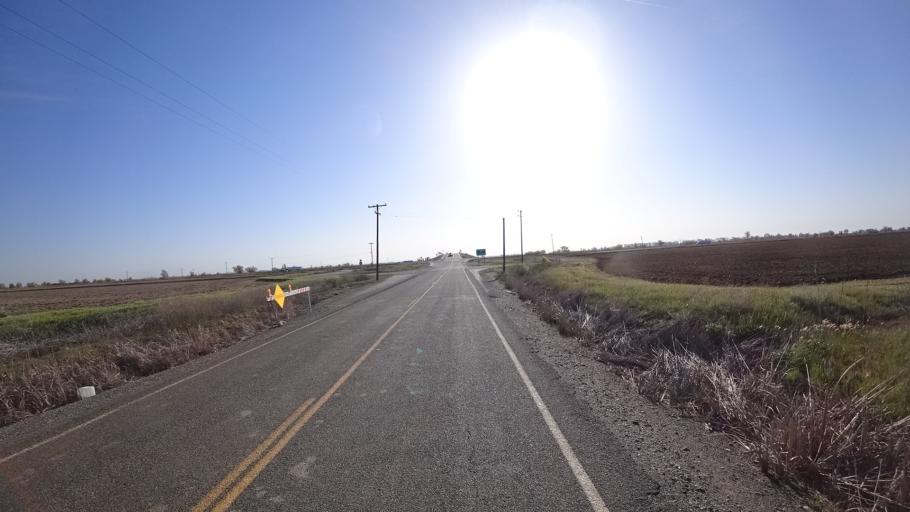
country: US
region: California
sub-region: Glenn County
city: Willows
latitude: 39.4071
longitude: -122.1999
